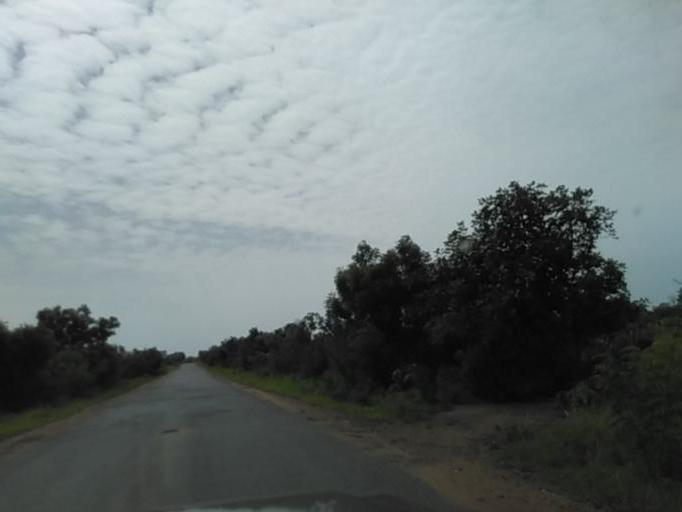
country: GH
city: Akropong
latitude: 6.0932
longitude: 0.0641
